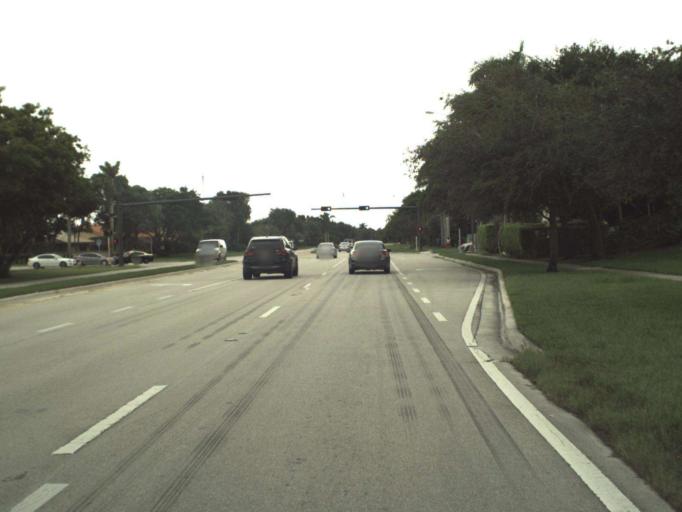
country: US
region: Florida
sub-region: Broward County
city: Coral Springs
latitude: 26.2371
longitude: -80.2826
